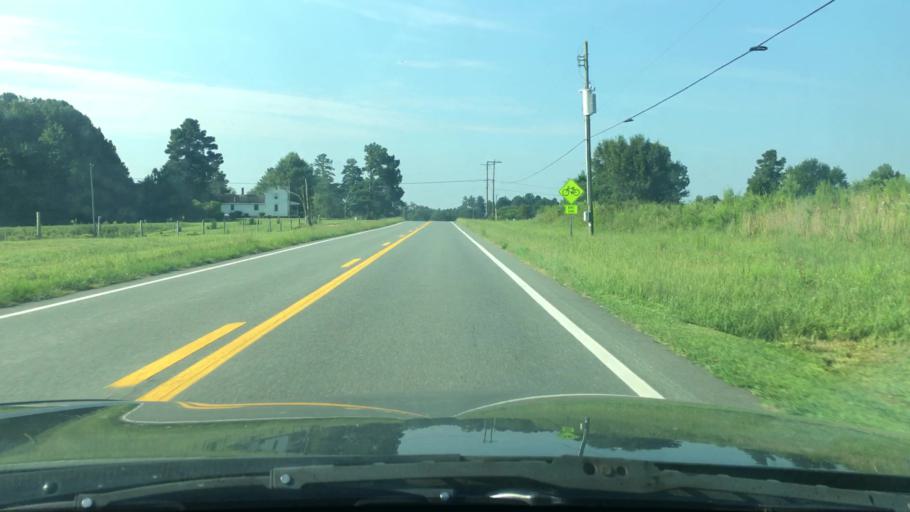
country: US
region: North Carolina
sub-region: Alamance County
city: Green Level
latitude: 36.2277
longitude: -79.3229
